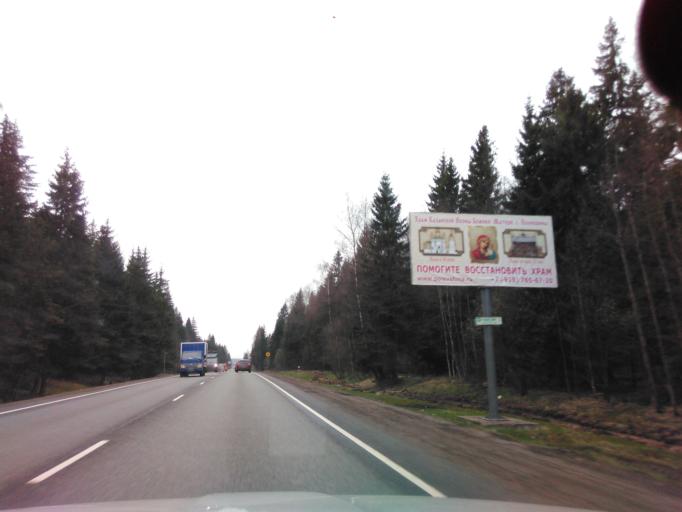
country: RU
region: Moskovskaya
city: Snegiri
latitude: 55.9463
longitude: 36.9688
